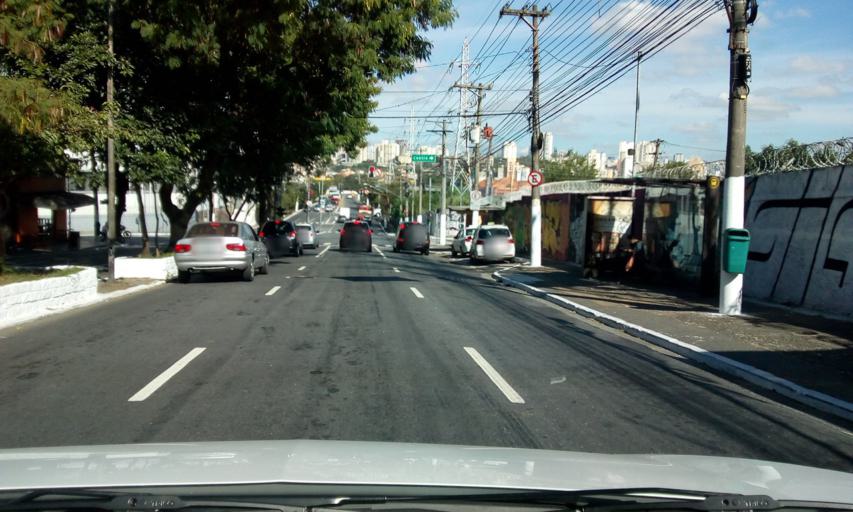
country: BR
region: Sao Paulo
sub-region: Sao Paulo
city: Sao Paulo
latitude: -23.5660
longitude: -46.6012
